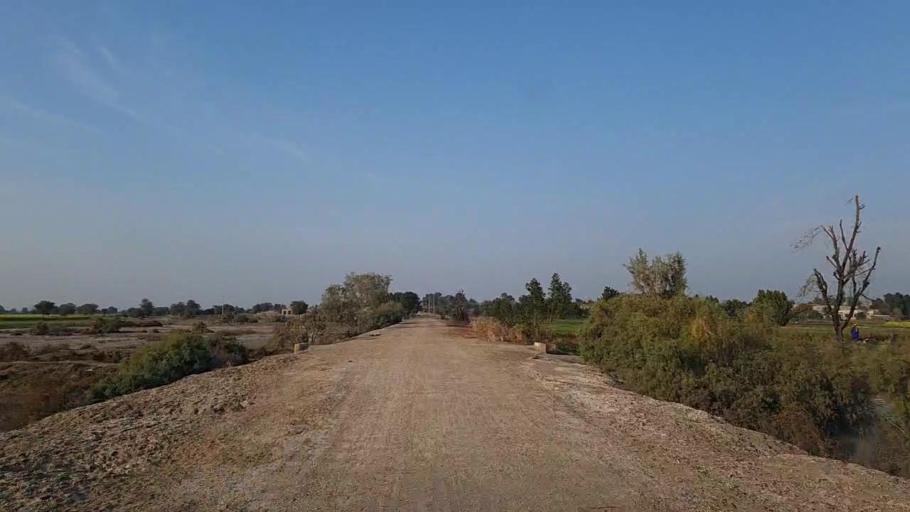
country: PK
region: Sindh
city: Jam Sahib
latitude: 26.3789
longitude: 68.5287
